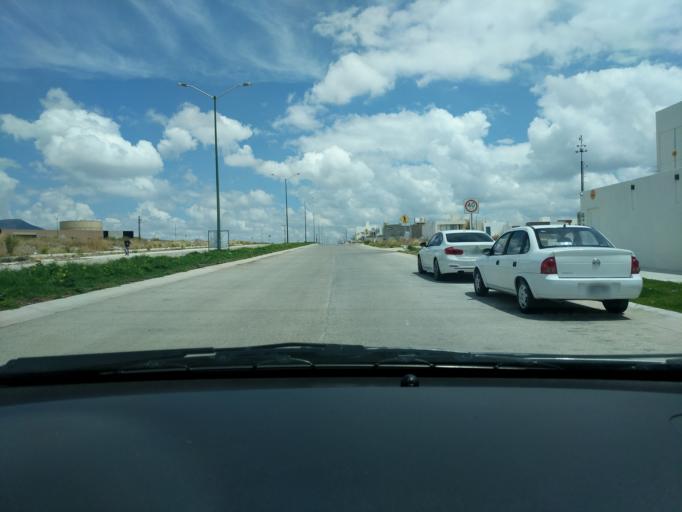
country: MX
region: San Luis Potosi
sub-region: Mexquitic de Carmona
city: Guadalupe Victoria
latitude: 22.1574
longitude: -101.0536
